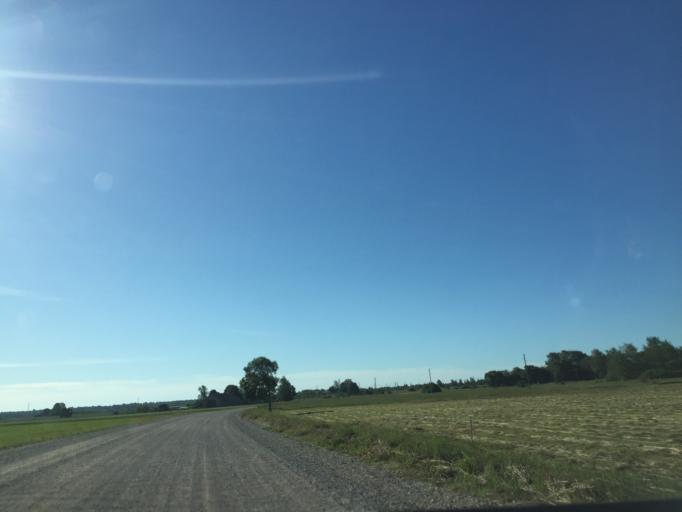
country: LV
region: Ventspils Rajons
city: Piltene
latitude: 57.3281
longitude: 21.6806
